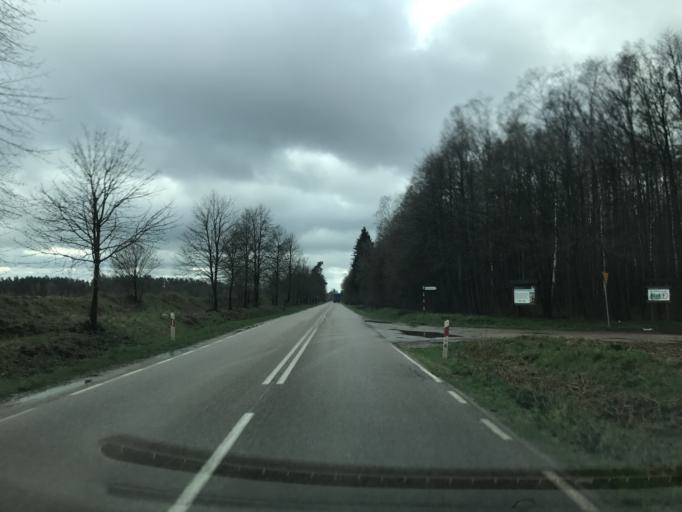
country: PL
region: Warmian-Masurian Voivodeship
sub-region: Powiat olsztynski
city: Olsztynek
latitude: 53.5198
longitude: 20.2206
